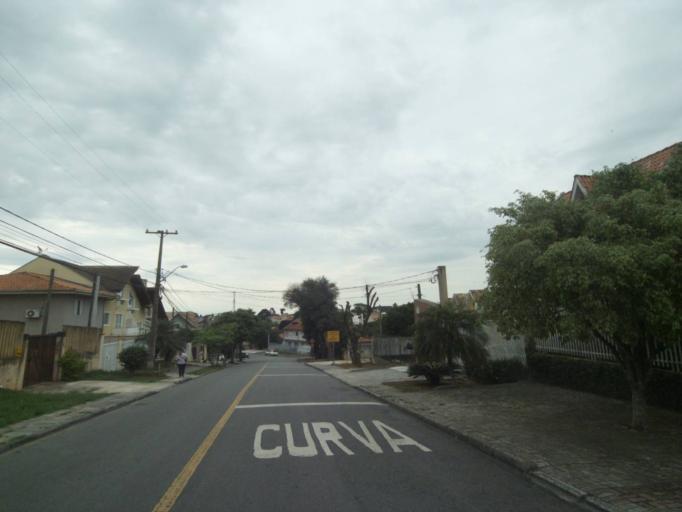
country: BR
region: Parana
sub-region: Curitiba
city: Curitiba
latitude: -25.3964
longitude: -49.2886
